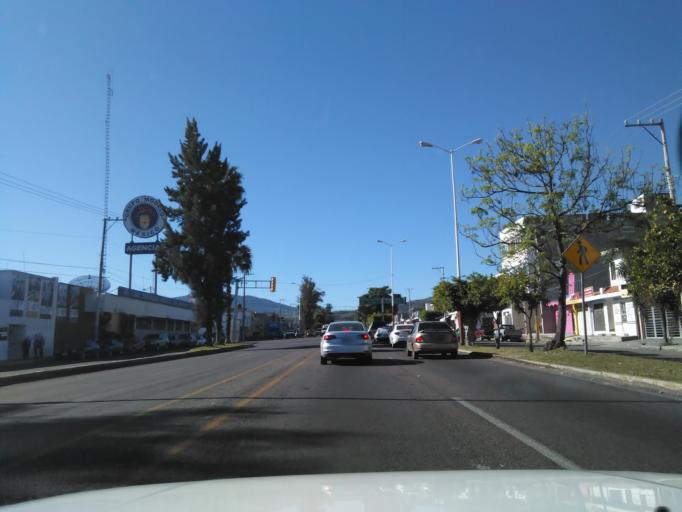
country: MX
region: Nayarit
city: Xalisco
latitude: 21.4560
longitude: -104.8958
